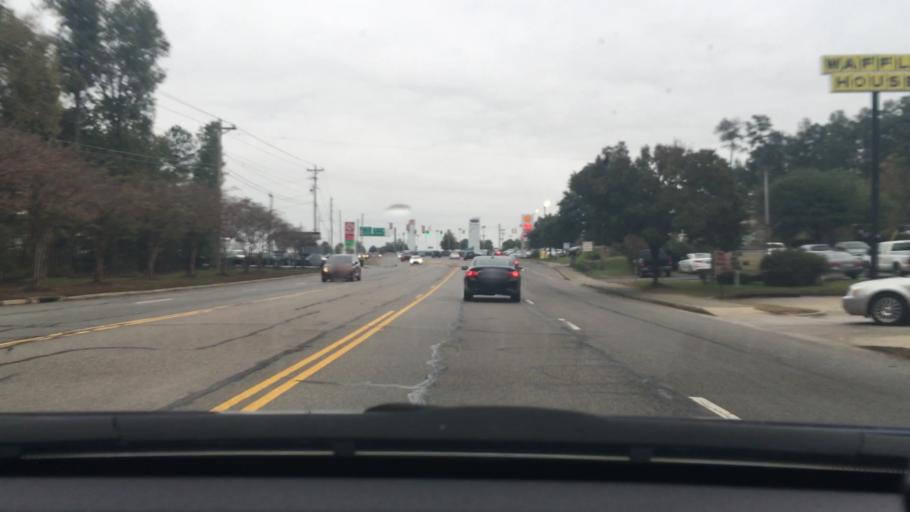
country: US
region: South Carolina
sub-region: Lexington County
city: Irmo
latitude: 34.1008
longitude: -81.1799
